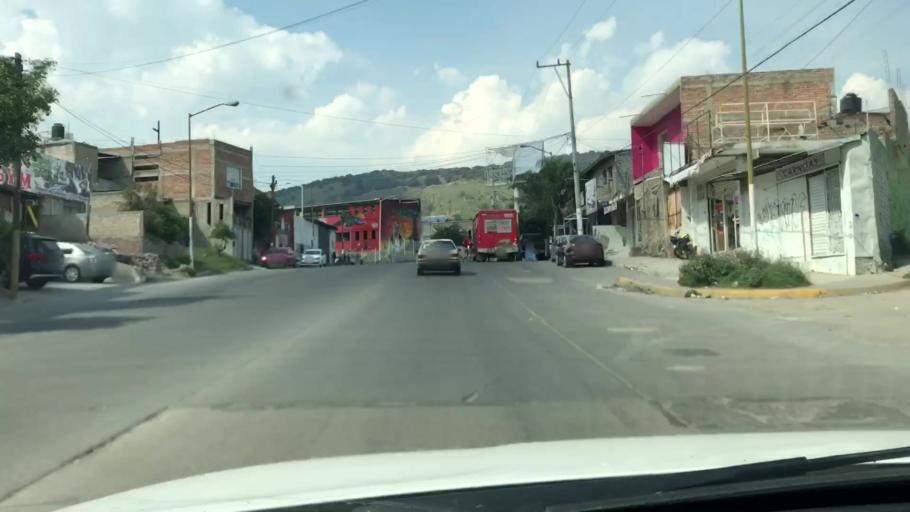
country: MX
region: Jalisco
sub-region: Tlajomulco de Zuniga
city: Palomar
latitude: 20.6397
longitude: -103.4609
